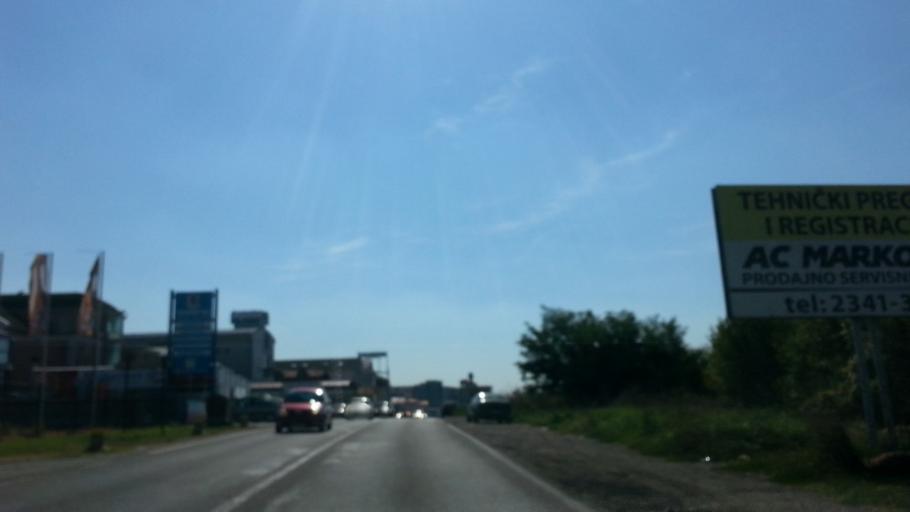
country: RS
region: Central Serbia
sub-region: Belgrade
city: Rakovica
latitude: 44.7284
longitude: 20.4199
